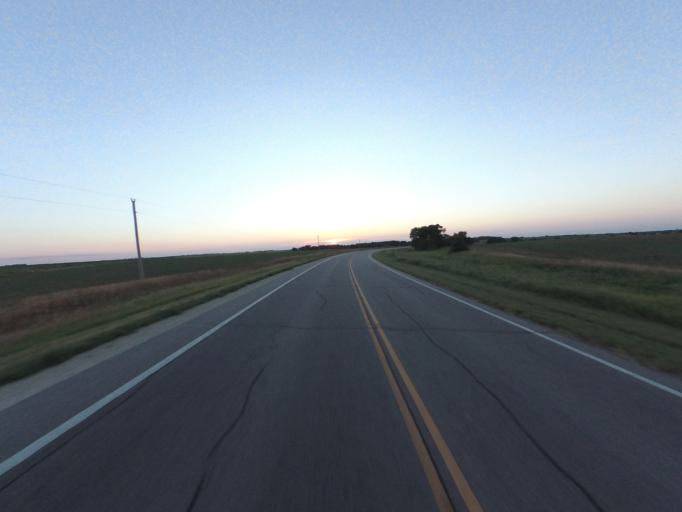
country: US
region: Kansas
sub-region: Rice County
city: Sterling
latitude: 38.1452
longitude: -98.2011
